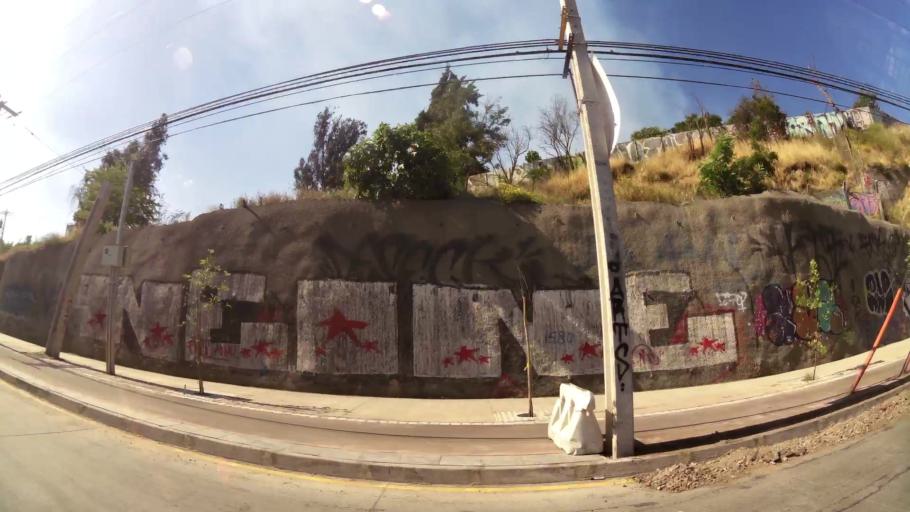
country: CL
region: Santiago Metropolitan
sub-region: Provincia de Santiago
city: Lo Prado
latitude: -33.5088
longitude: -70.7701
